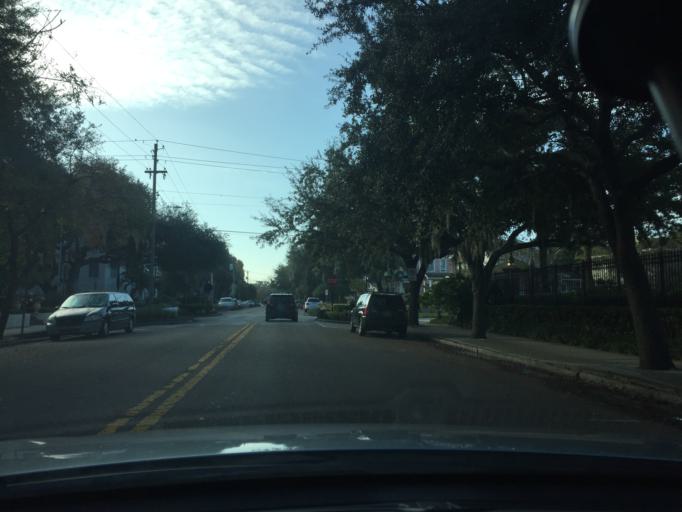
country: US
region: Florida
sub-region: Hillsborough County
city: Tampa
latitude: 27.9341
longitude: -82.4769
